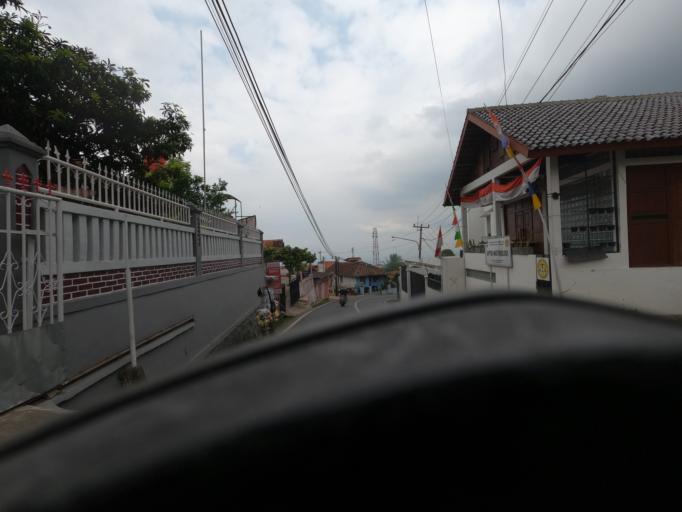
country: ID
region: West Java
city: Cimahi
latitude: -6.8194
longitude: 107.5377
